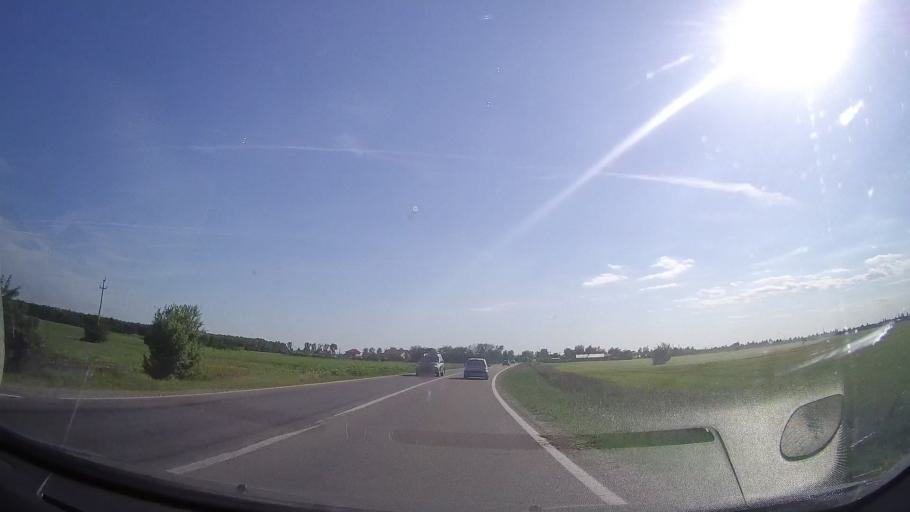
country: RO
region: Prahova
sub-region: Comuna Berceni
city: Corlatesti
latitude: 44.9181
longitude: 26.1005
